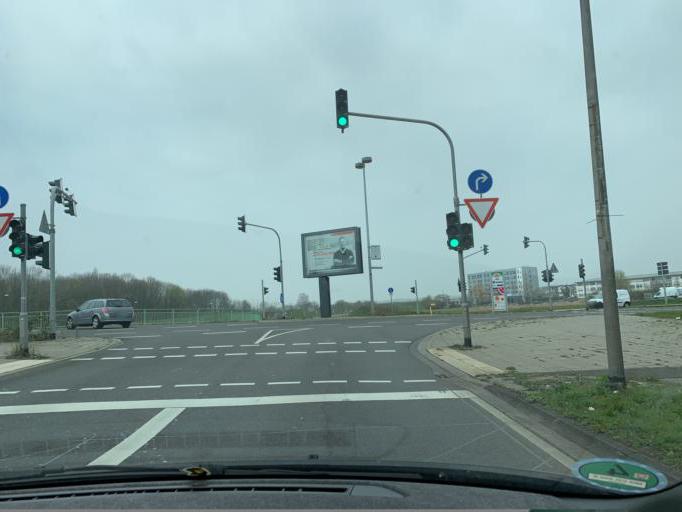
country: DE
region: North Rhine-Westphalia
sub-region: Regierungsbezirk Koln
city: Bilderstoeckchen
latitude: 51.0308
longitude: 6.9184
